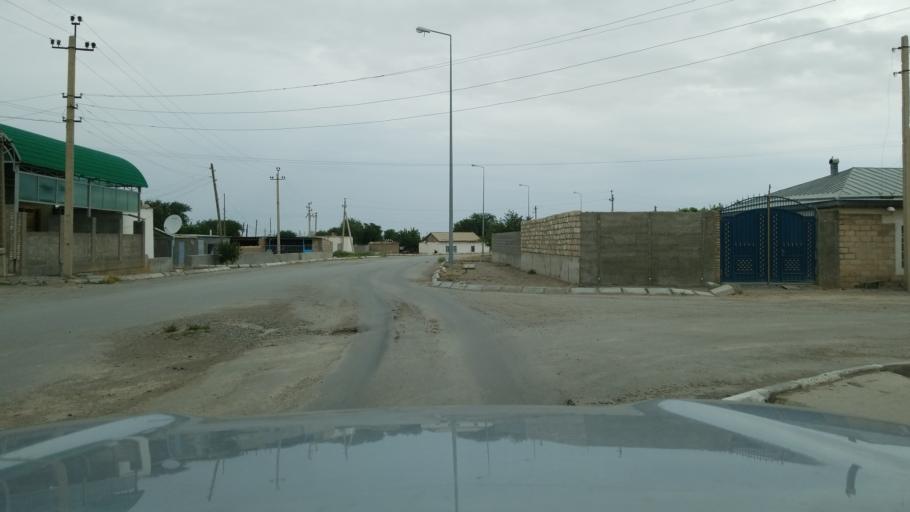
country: TM
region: Balkan
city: Serdar
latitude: 38.9857
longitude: 56.2756
